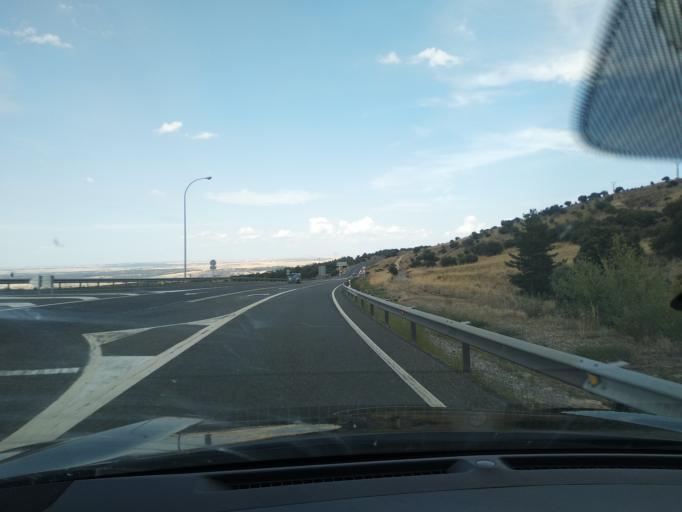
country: ES
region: Castille and Leon
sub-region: Provincia de Segovia
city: Otero de Herreros
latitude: 40.7906
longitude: -4.2154
